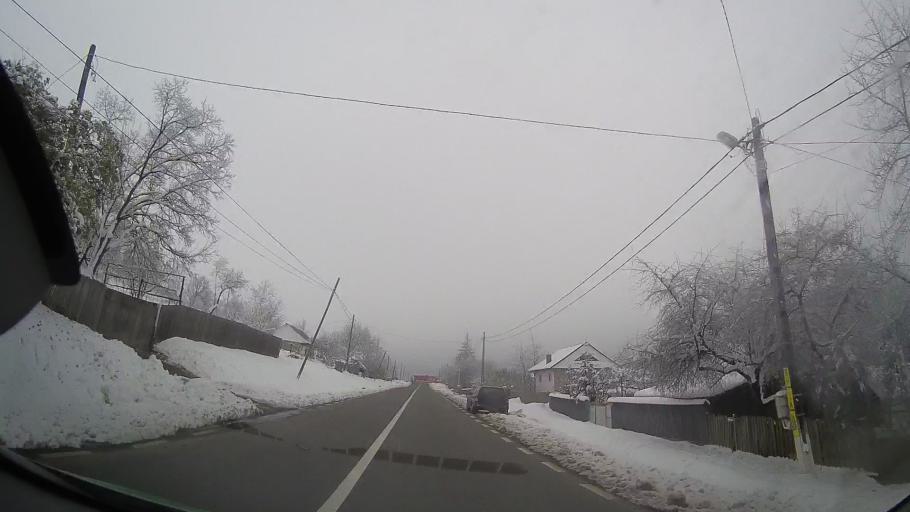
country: RO
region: Neamt
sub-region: Comuna Poenari
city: Poienari
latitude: 46.8812
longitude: 27.1320
